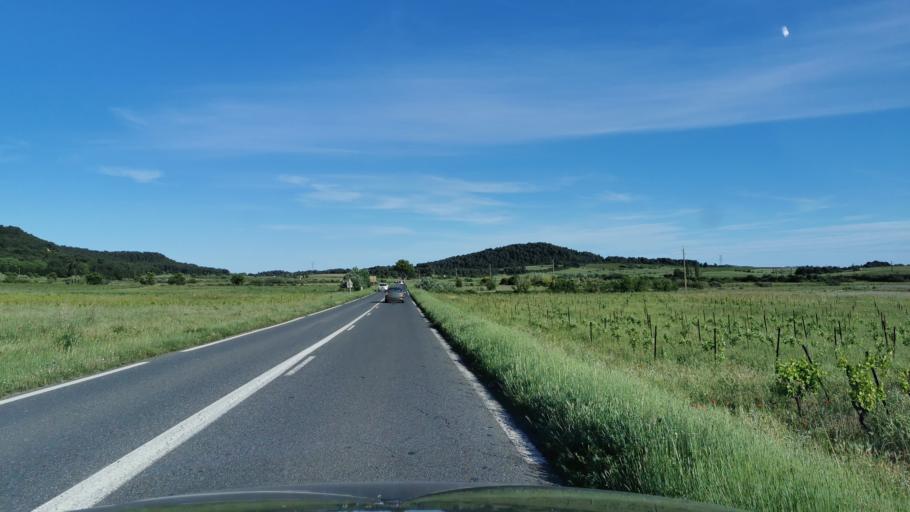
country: FR
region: Languedoc-Roussillon
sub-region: Departement de l'Aude
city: Marcorignan
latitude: 43.2163
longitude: 2.9306
